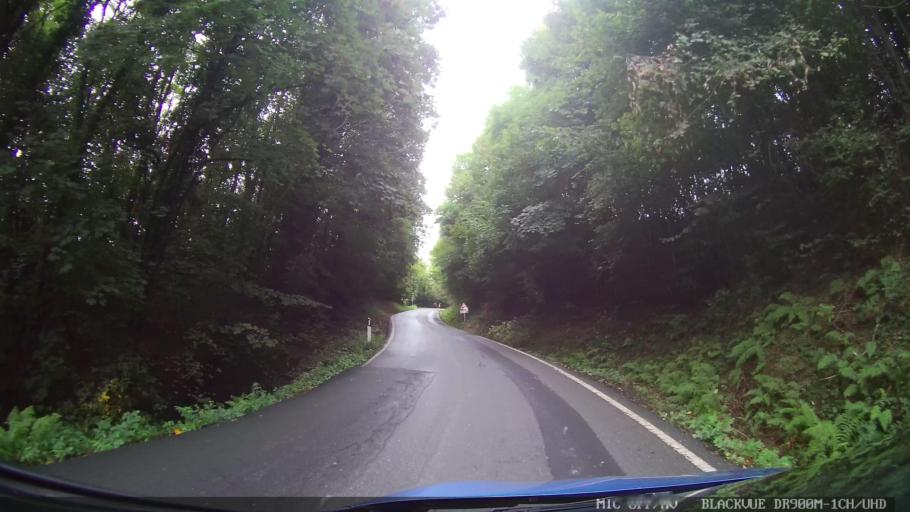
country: IT
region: Piedmont
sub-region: Provincia di Torino
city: Levone
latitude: 45.3293
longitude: 7.6218
